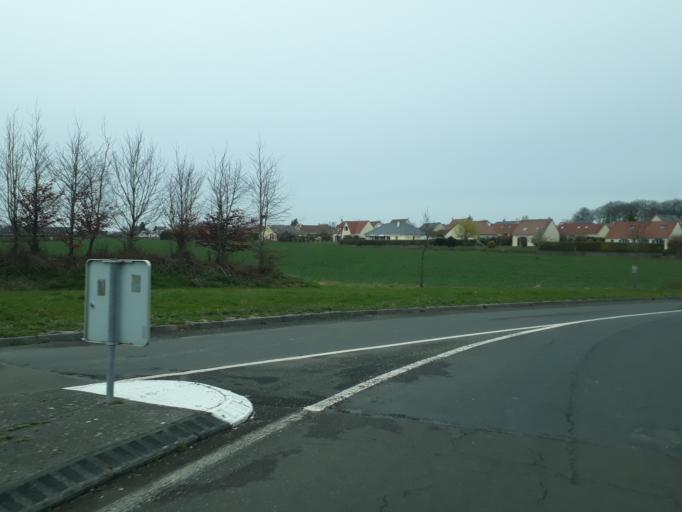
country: FR
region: Haute-Normandie
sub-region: Departement de la Seine-Maritime
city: Goderville
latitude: 49.6377
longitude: 0.3614
